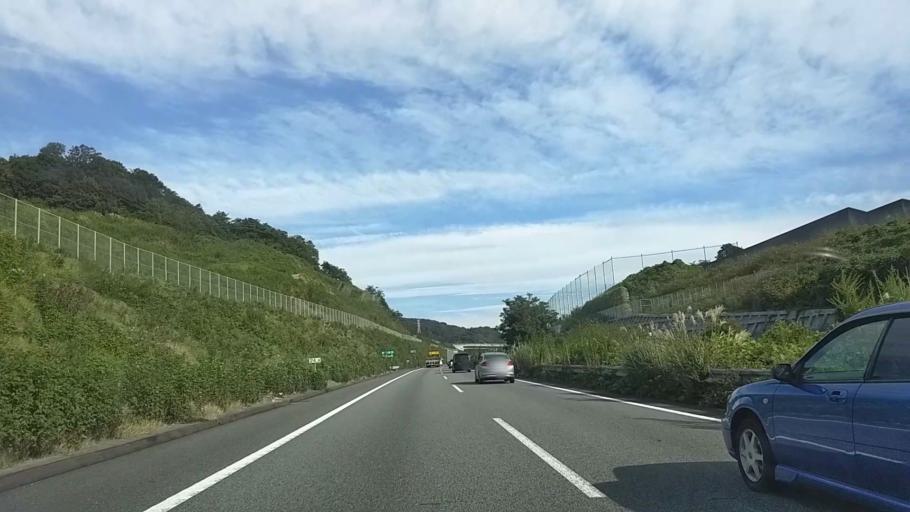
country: JP
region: Kanagawa
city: Zama
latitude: 35.5395
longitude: 139.3233
